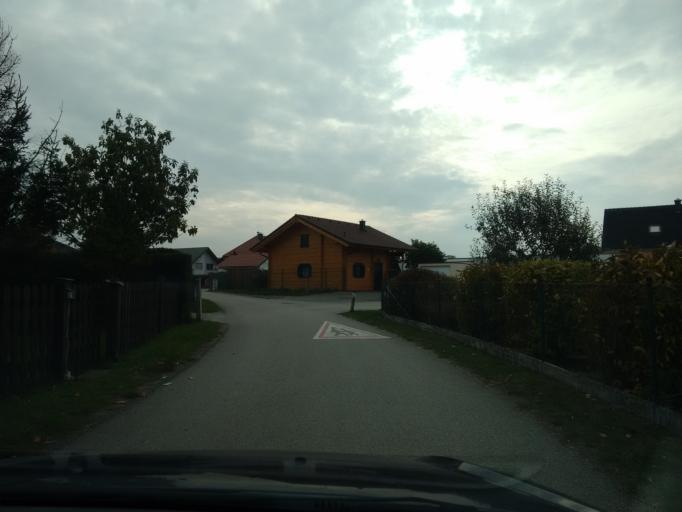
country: AT
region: Upper Austria
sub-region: Wels-Land
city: Offenhausen
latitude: 48.1704
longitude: 13.8698
